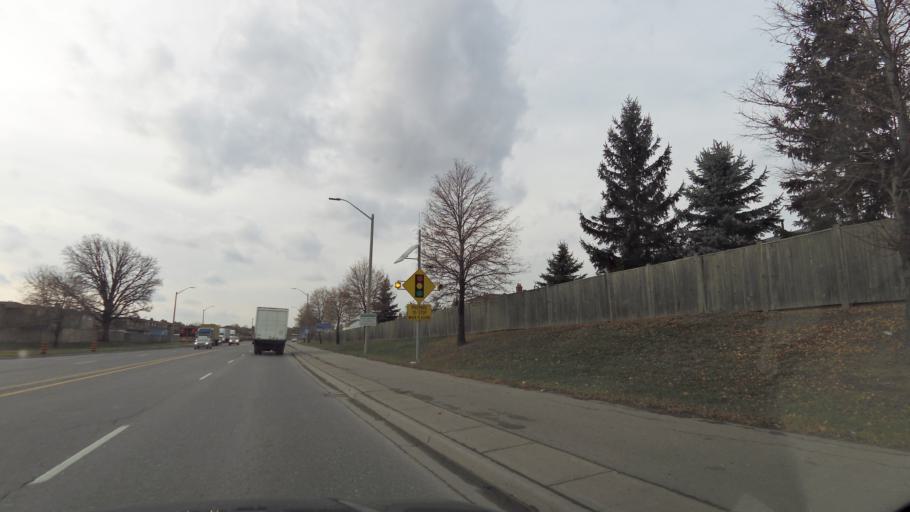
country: CA
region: Ontario
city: Etobicoke
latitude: 43.7337
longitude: -79.6297
